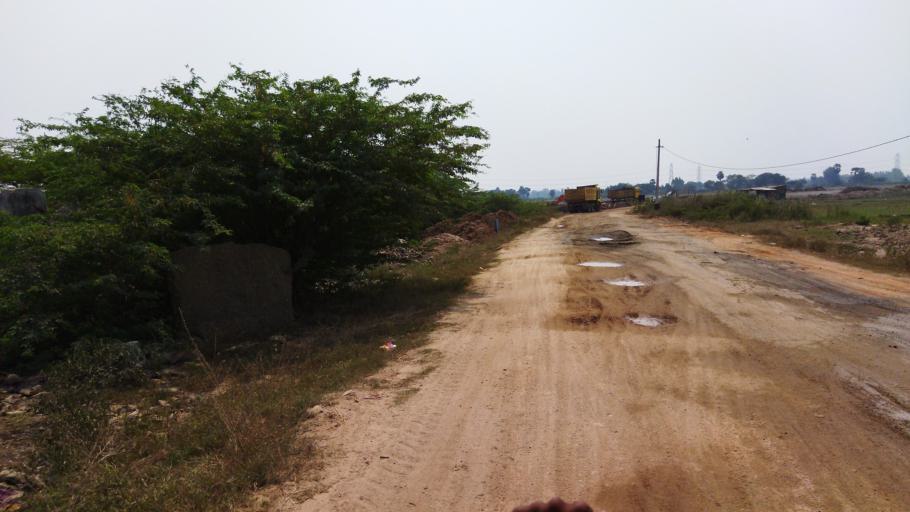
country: IN
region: Telangana
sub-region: Nalgonda
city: Nalgonda
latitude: 17.1386
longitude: 79.3857
